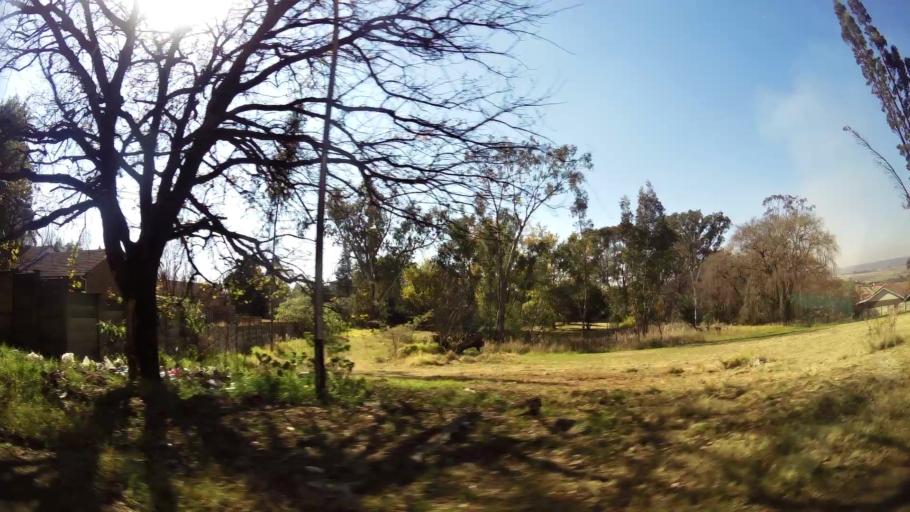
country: ZA
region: Mpumalanga
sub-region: Nkangala District Municipality
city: Witbank
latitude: -25.8292
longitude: 29.2452
